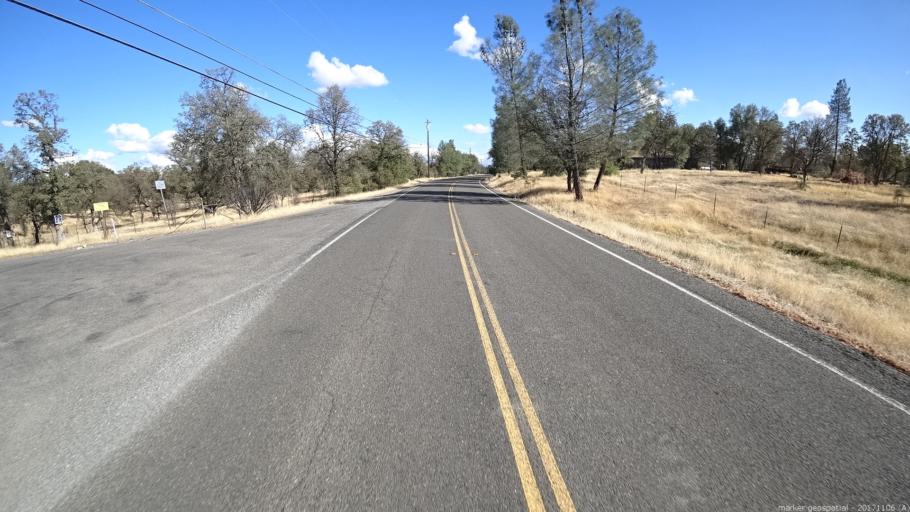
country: US
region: California
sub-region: Shasta County
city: Palo Cedro
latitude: 40.5926
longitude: -122.2710
